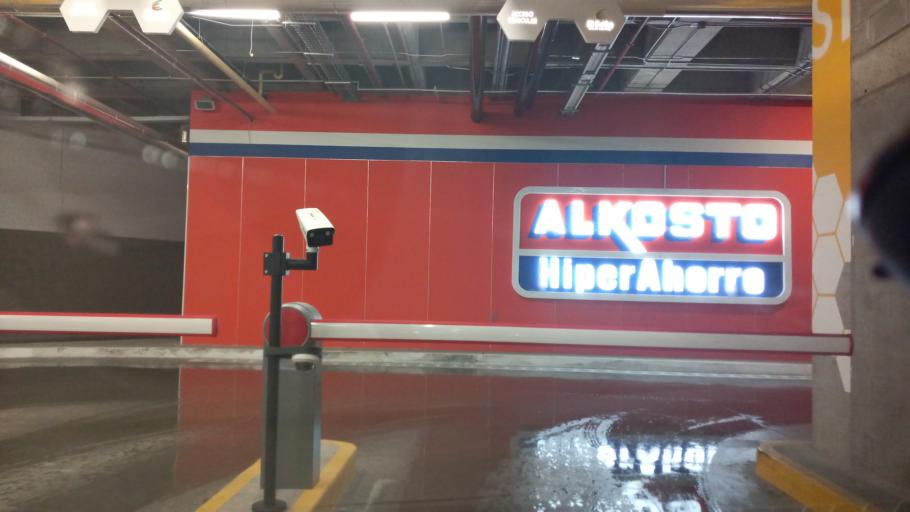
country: CO
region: Bogota D.C.
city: Bogota
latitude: 4.6466
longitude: -74.1281
